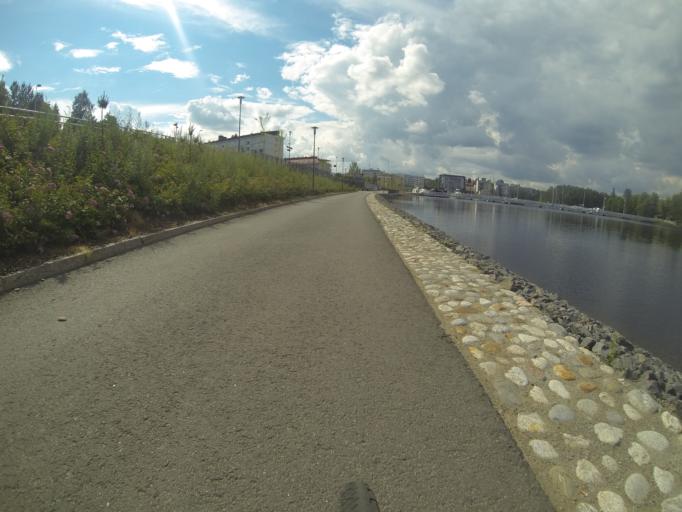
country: FI
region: Southern Savonia
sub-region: Savonlinna
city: Savonlinna
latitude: 61.8689
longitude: 28.8899
